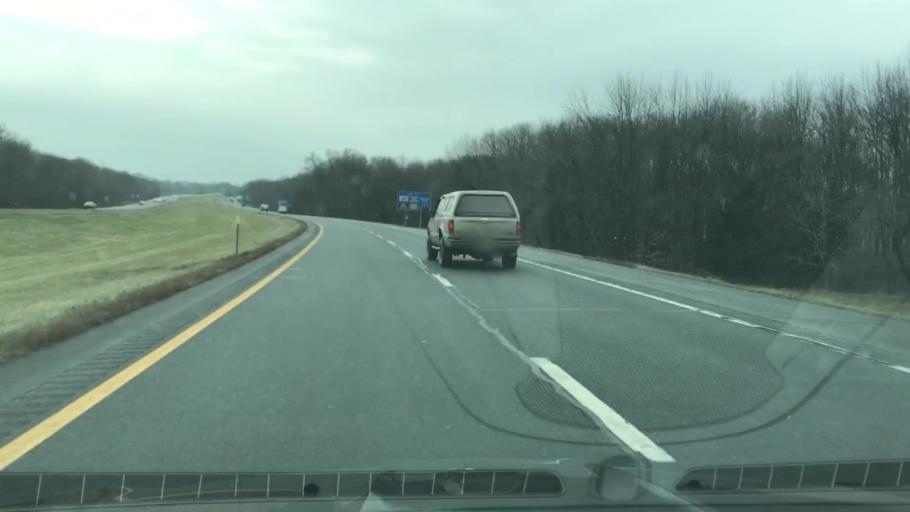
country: US
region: New York
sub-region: Orange County
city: Maybrook
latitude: 41.5169
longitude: -74.1938
